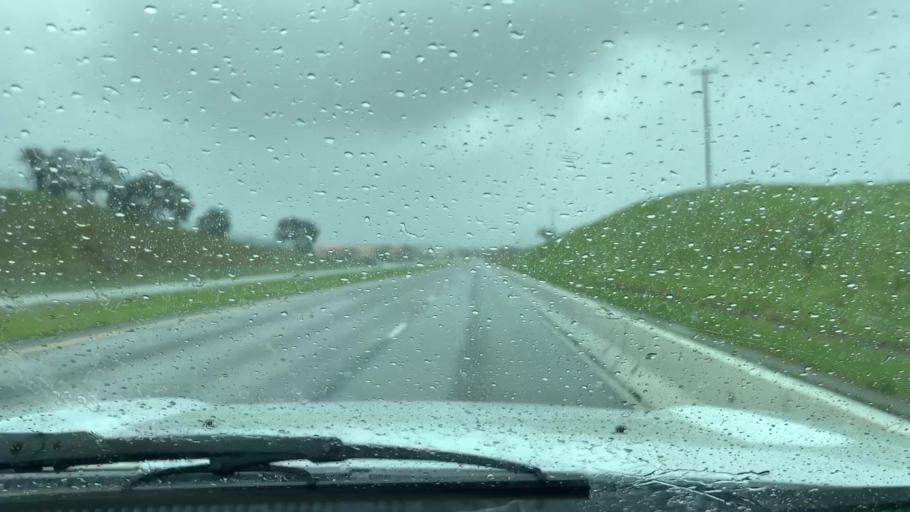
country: US
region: California
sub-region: San Luis Obispo County
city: Paso Robles
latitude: 35.6510
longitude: -120.6239
